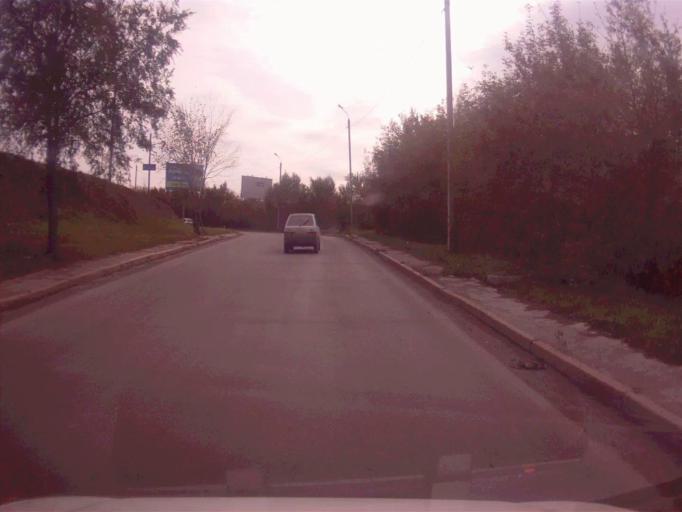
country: RU
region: Chelyabinsk
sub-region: Gorod Chelyabinsk
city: Chelyabinsk
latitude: 55.1605
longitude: 61.4282
